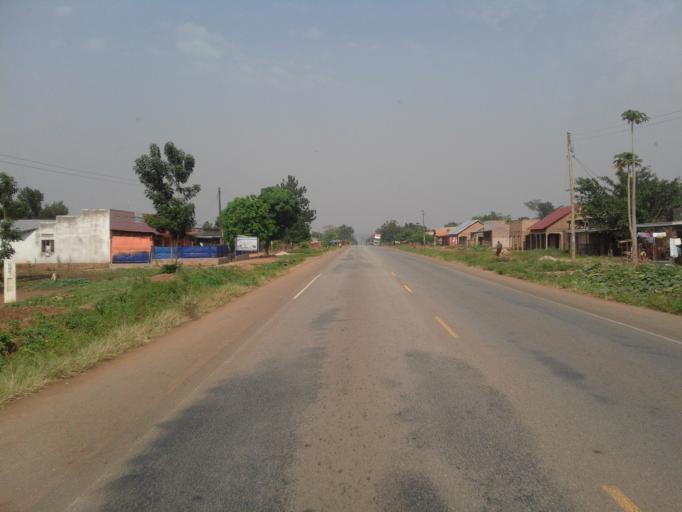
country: UG
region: Eastern Region
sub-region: Bugiri District
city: Bugiri
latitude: 0.6048
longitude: 33.6891
